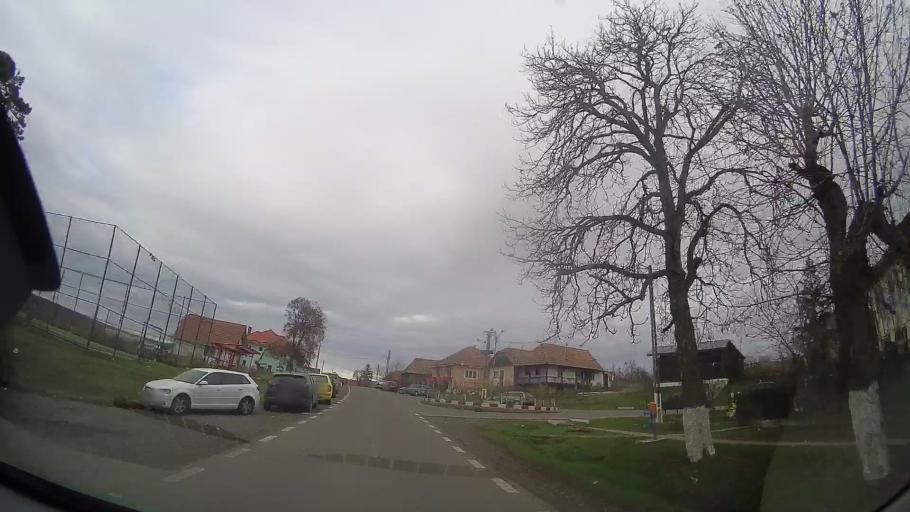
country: RO
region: Mures
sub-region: Comuna Faragau
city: Faragau
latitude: 46.7805
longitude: 24.5523
